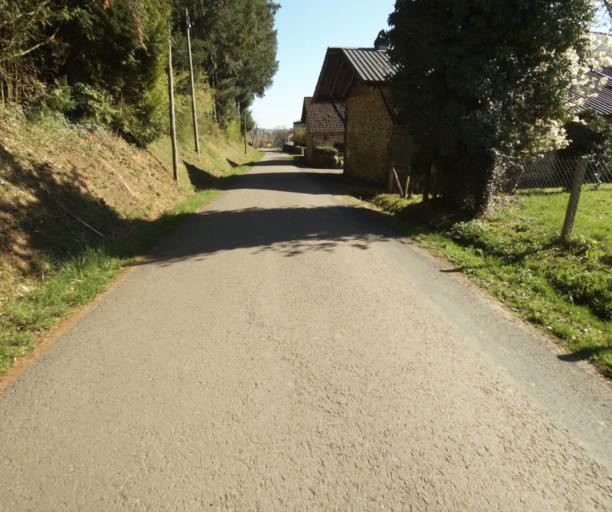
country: FR
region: Limousin
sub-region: Departement de la Correze
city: Tulle
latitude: 45.2797
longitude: 1.7208
